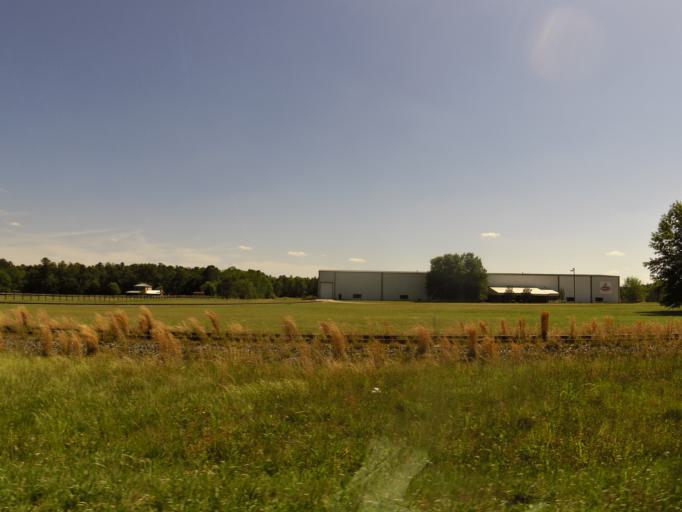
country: US
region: South Carolina
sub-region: Aiken County
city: Aiken
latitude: 33.5228
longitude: -81.6139
